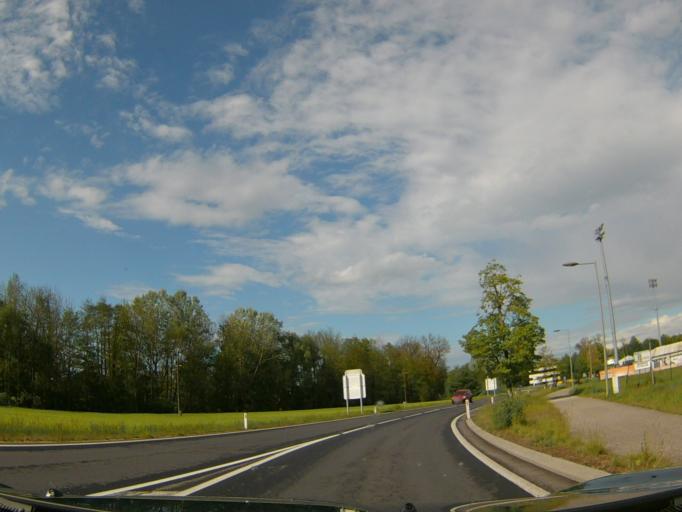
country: AT
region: Upper Austria
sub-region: Politischer Bezirk Vocklabruck
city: Schwanenstadt
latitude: 48.0486
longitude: 13.7808
